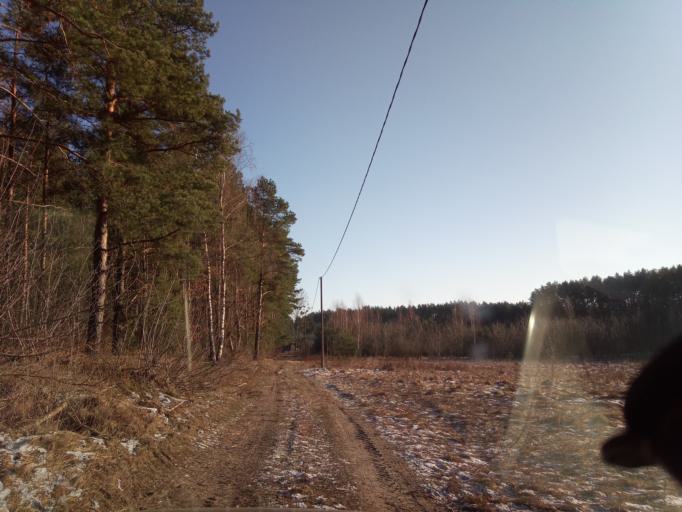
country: LT
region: Alytaus apskritis
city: Druskininkai
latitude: 53.9492
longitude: 23.8745
